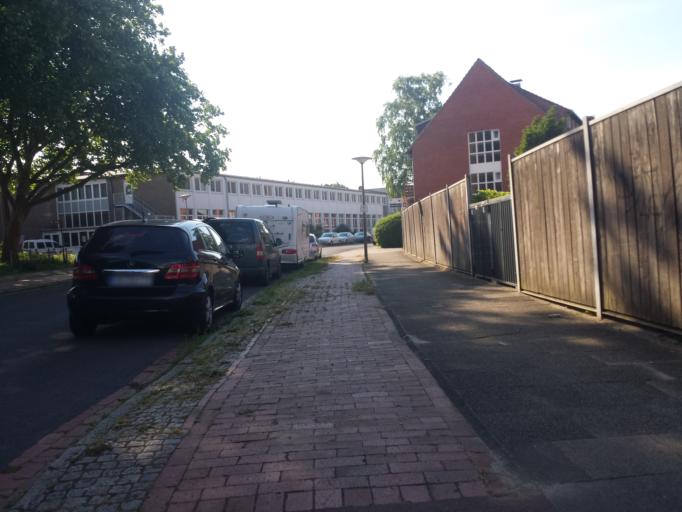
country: DE
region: Lower Saxony
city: Lilienthal
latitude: 53.0694
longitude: 8.8864
